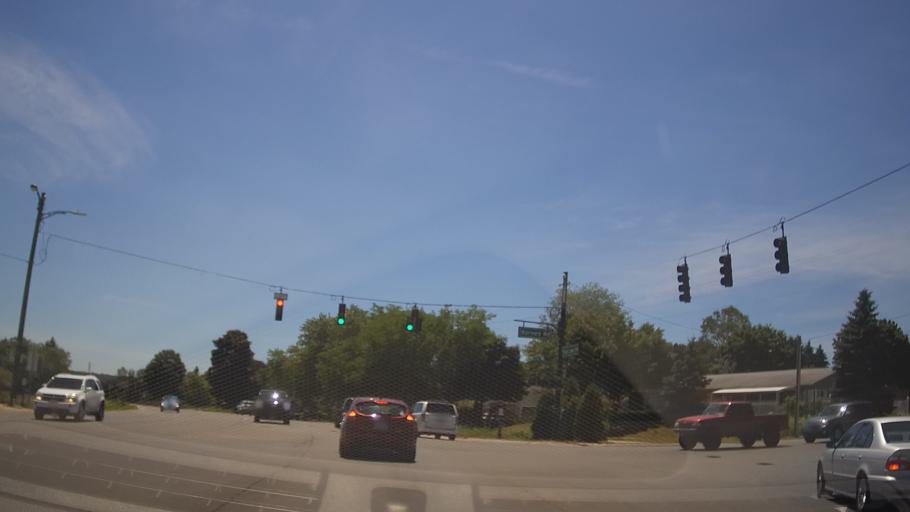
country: US
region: Michigan
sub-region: Grand Traverse County
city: Traverse City
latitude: 44.7430
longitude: -85.6553
